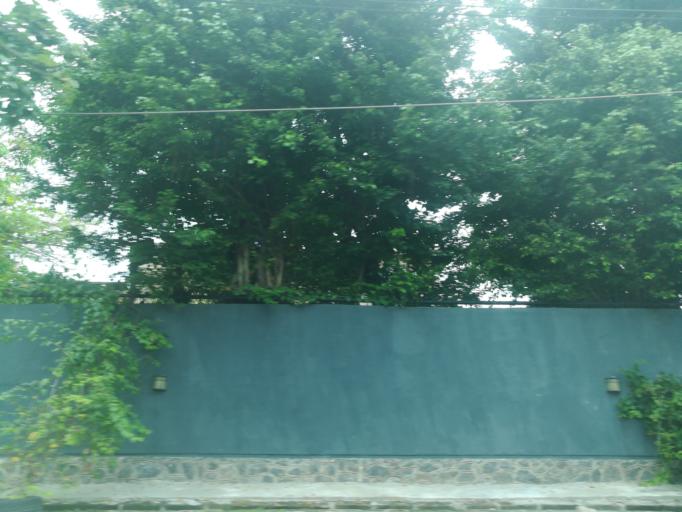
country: NG
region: Lagos
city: Ikoyi
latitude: 6.4326
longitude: 3.4152
